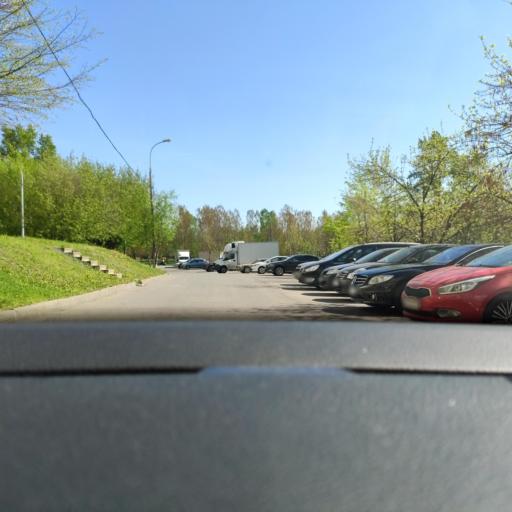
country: RU
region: Moscow
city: Kozeyevo
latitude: 55.8709
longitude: 37.6269
